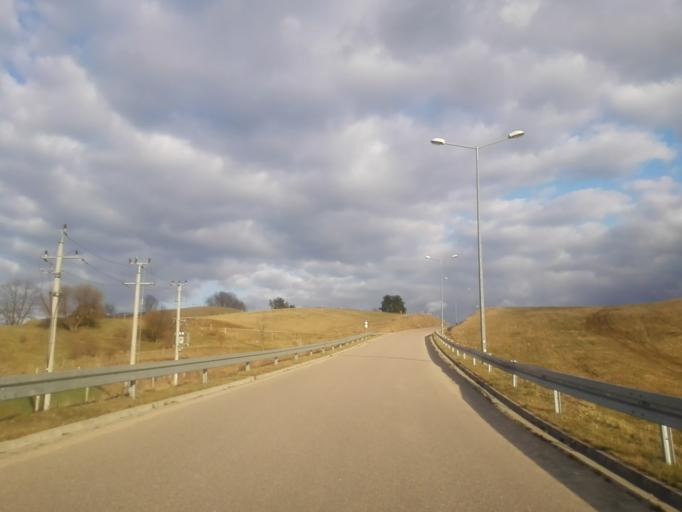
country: PL
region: Podlasie
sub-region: Suwalki
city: Suwalki
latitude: 54.2096
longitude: 22.9727
